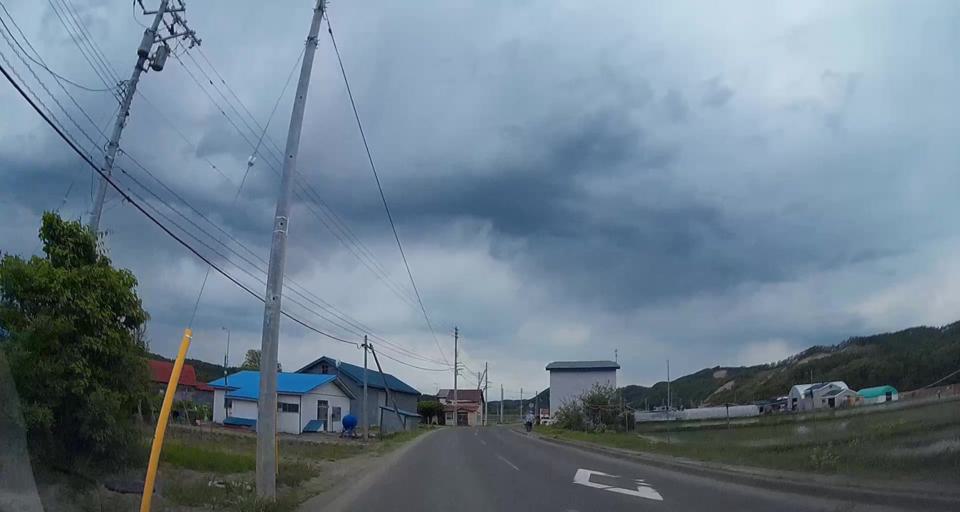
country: JP
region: Hokkaido
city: Chitose
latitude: 42.7548
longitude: 141.9772
